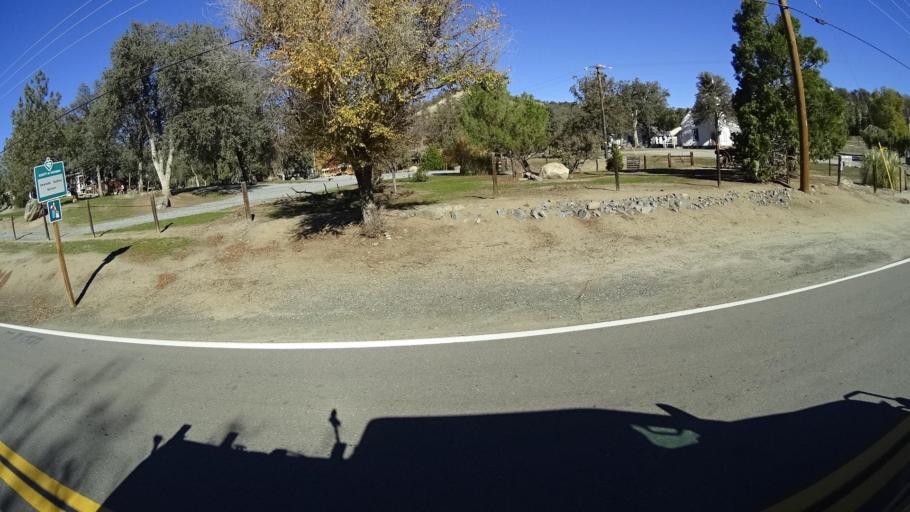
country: US
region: California
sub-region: Kern County
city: Alta Sierra
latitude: 35.7289
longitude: -118.7044
